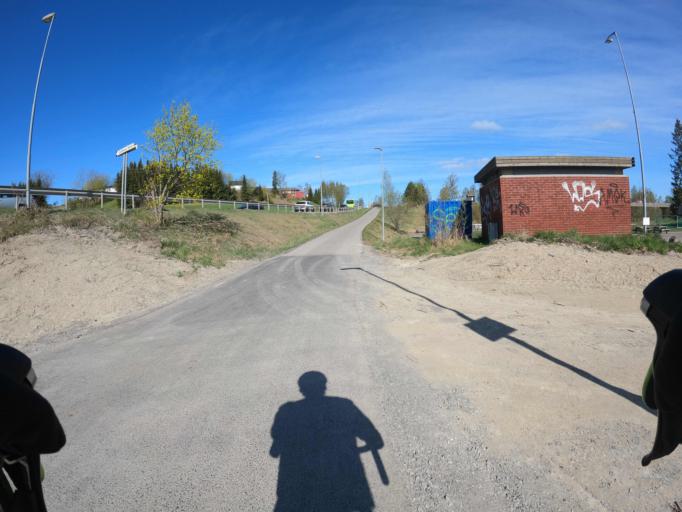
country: NO
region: Akershus
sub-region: Lorenskog
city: Kjenn
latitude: 59.9676
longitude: 10.9934
